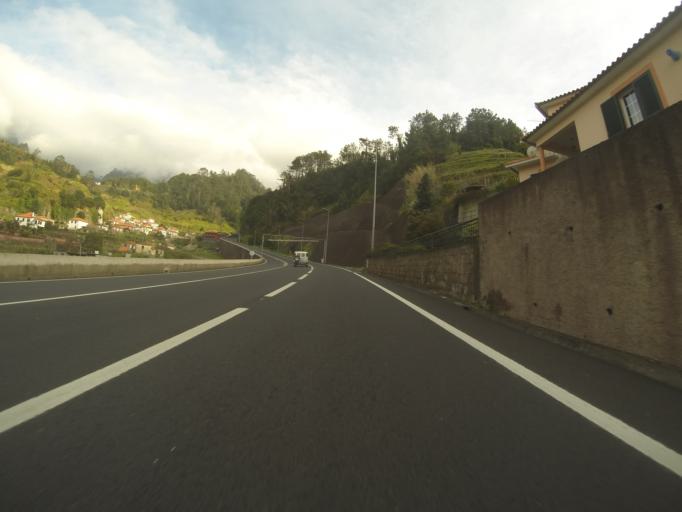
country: PT
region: Madeira
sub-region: Sao Vicente
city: Sao Vicente
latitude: 32.7734
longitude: -17.0312
